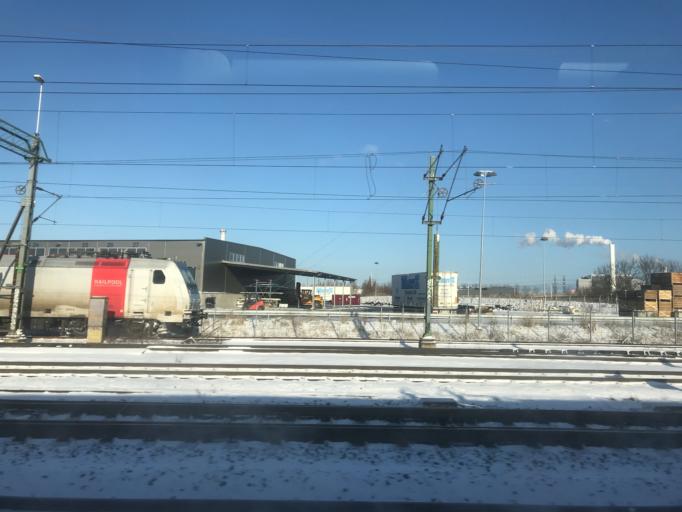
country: SE
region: Skane
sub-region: Burlovs Kommun
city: Arloev
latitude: 55.6230
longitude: 13.0527
